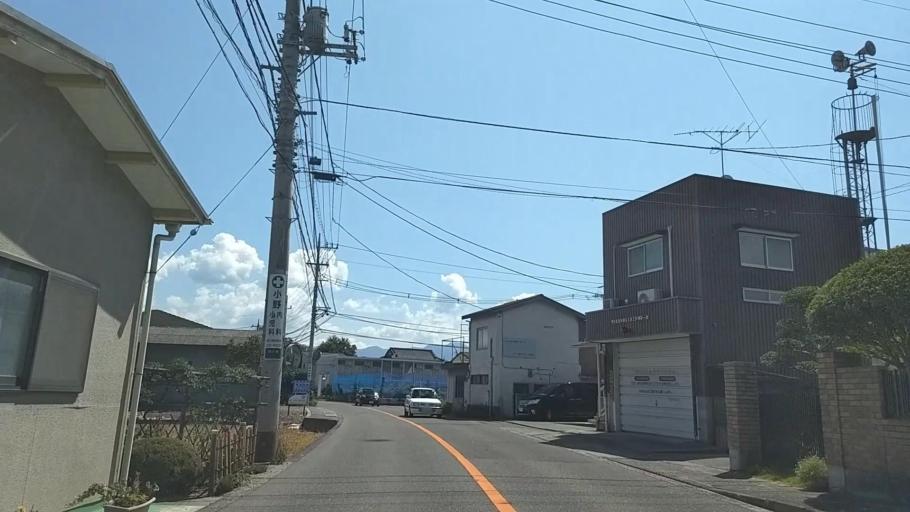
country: JP
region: Yamanashi
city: Ryuo
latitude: 35.6489
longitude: 138.5167
